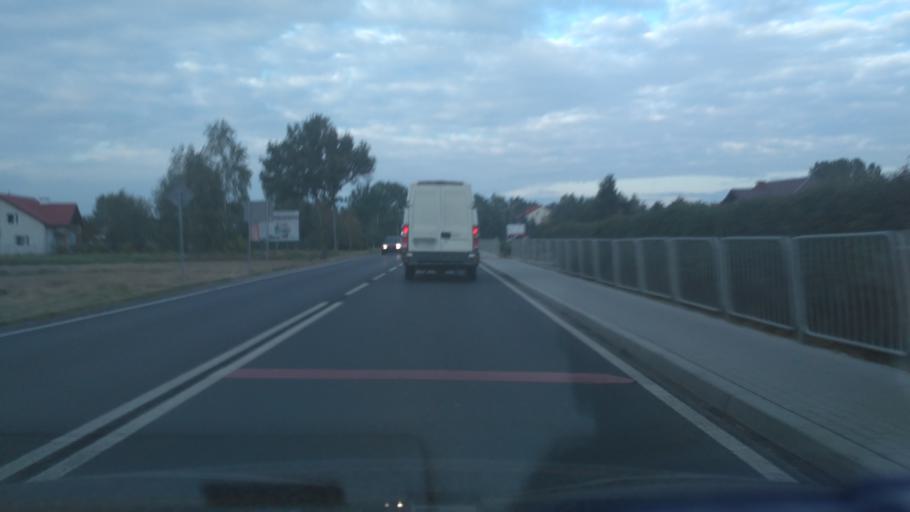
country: PL
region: Lublin Voivodeship
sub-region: Powiat leczynski
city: Spiczyn
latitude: 51.2983
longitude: 22.7197
